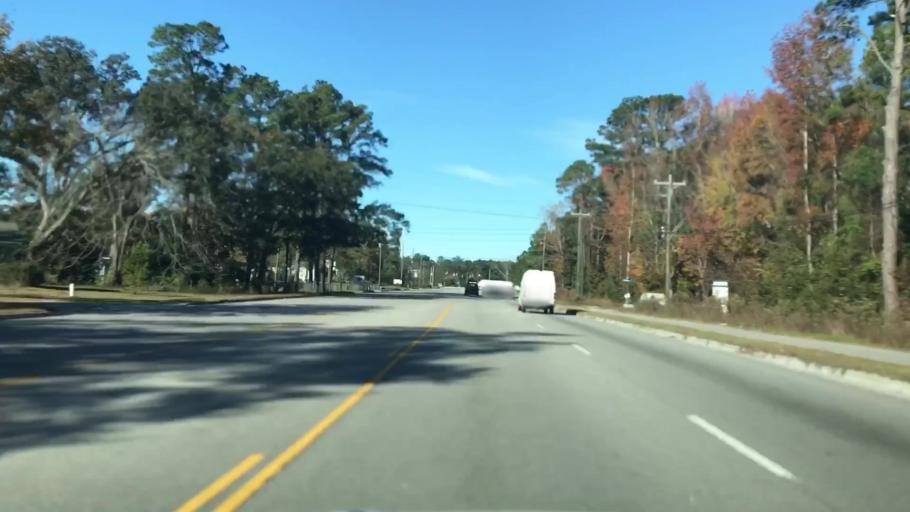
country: US
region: South Carolina
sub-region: Dorchester County
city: Centerville
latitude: 32.9692
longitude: -80.2057
